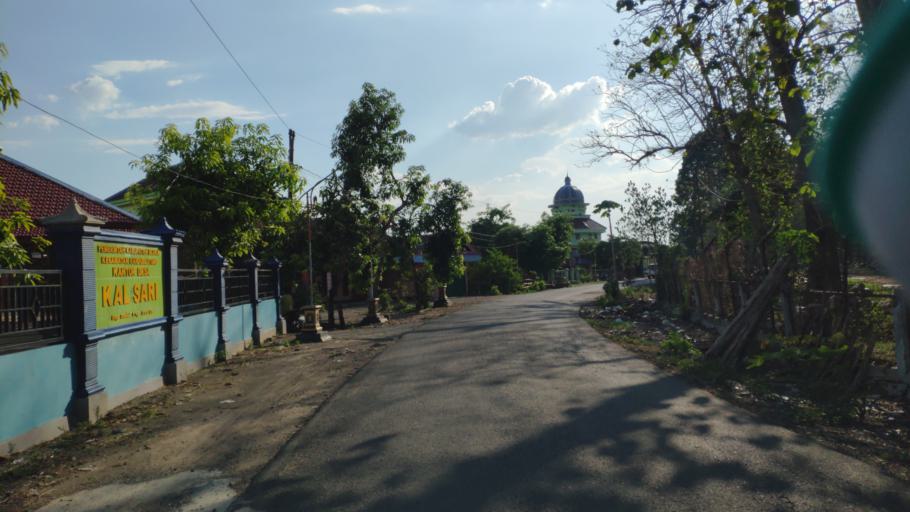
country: ID
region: Central Java
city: Ngliron
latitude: -7.1440
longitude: 111.4182
